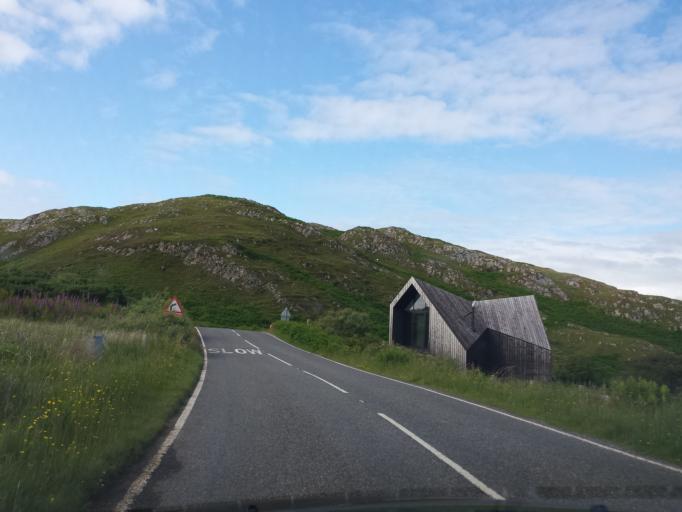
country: GB
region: Scotland
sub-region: Argyll and Bute
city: Isle Of Mull
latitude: 56.9586
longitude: -5.8415
